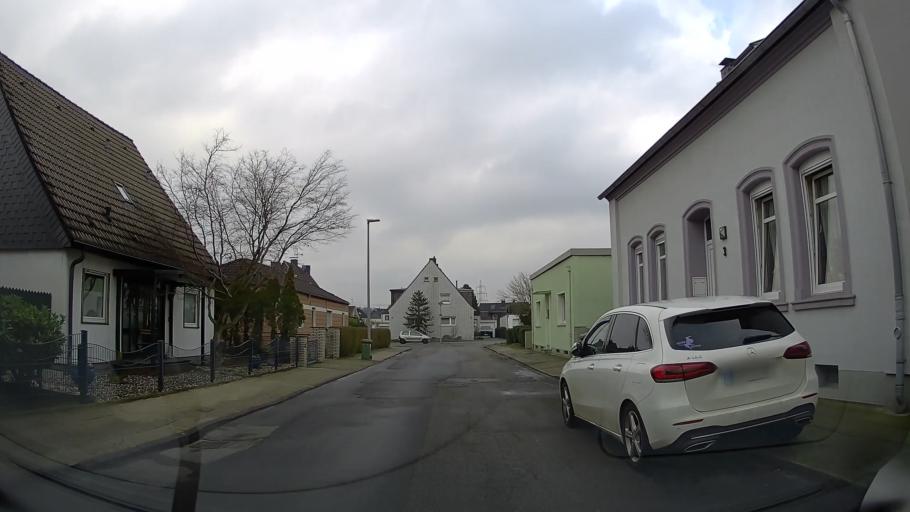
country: DE
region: North Rhine-Westphalia
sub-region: Regierungsbezirk Dusseldorf
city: Oberhausen
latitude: 51.4750
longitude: 6.8888
